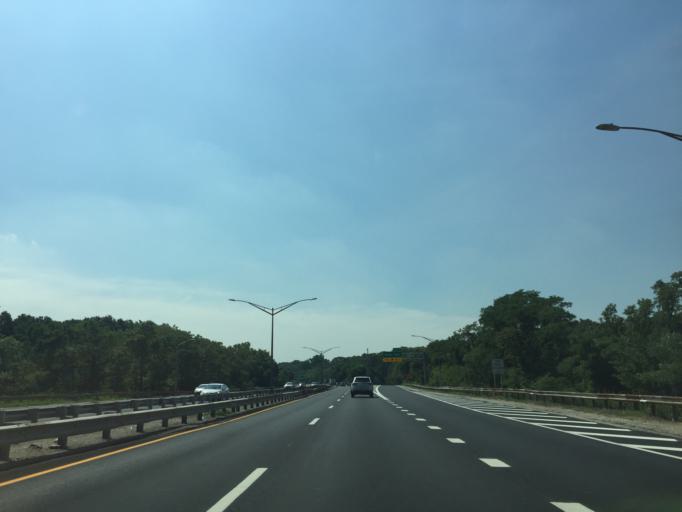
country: US
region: New York
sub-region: Nassau County
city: Bellerose Terrace
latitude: 40.7364
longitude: -73.7680
